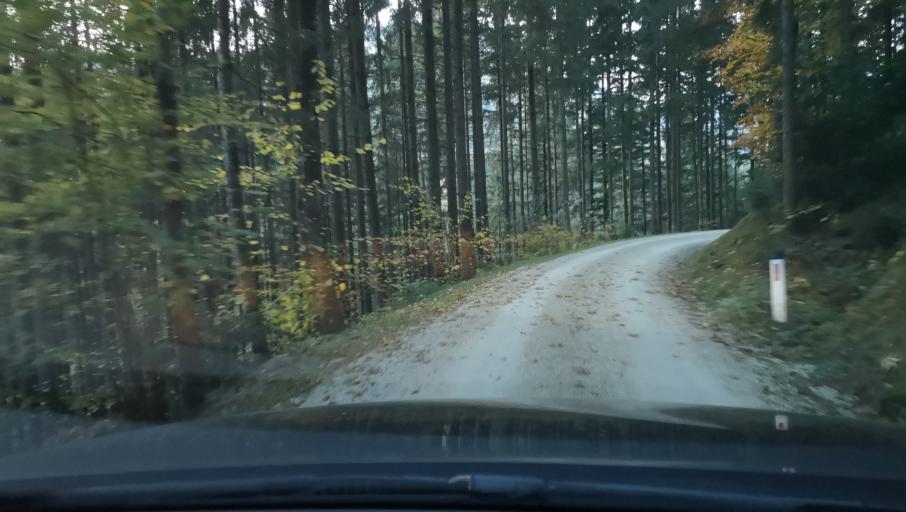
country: AT
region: Styria
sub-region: Politischer Bezirk Weiz
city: Birkfeld
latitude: 47.3653
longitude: 15.6565
